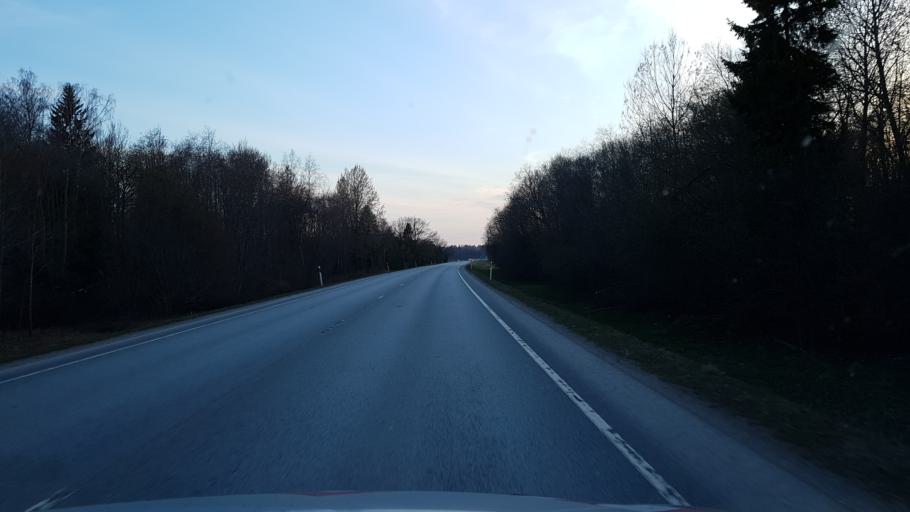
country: EE
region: Laeaene-Virumaa
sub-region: Rakvere linn
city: Rakvere
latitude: 59.3244
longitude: 26.3873
